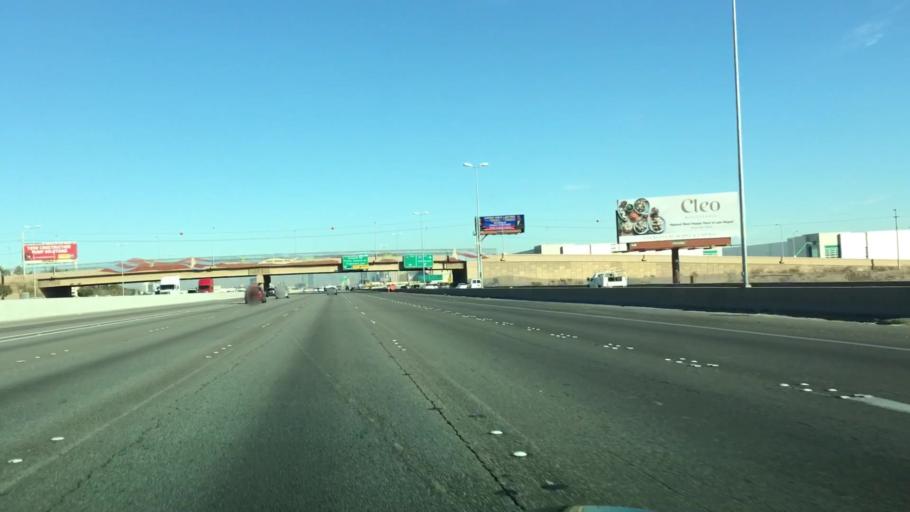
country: US
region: Nevada
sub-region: Clark County
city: Paradise
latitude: 36.0551
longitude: -115.1805
